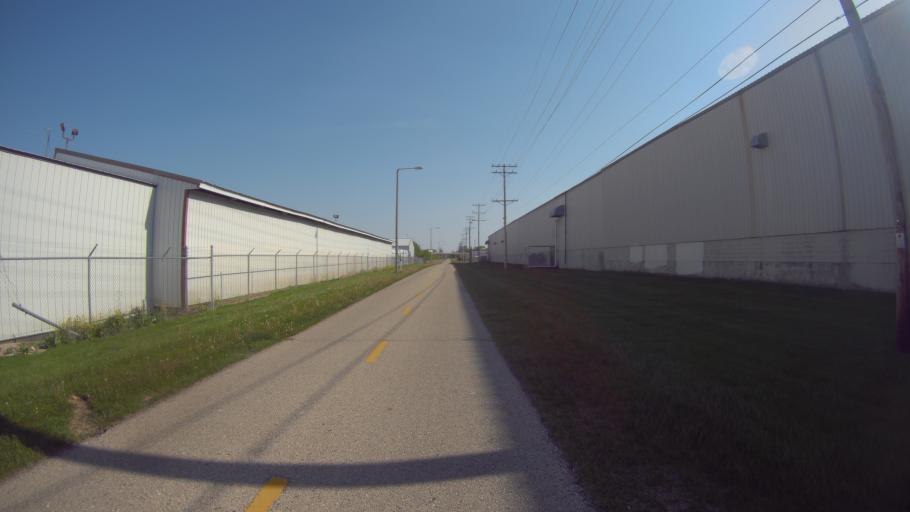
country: US
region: Wisconsin
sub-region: Dane County
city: Shorewood Hills
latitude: 43.0368
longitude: -89.4592
